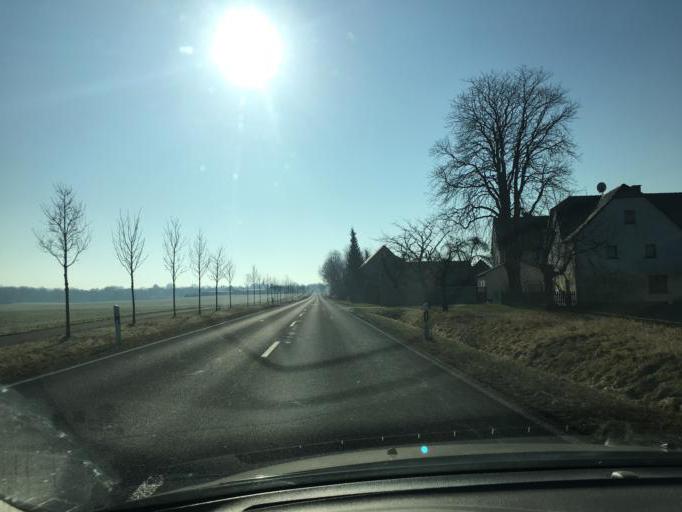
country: DE
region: Saxony
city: Bad Lausick
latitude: 51.1600
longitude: 12.6301
